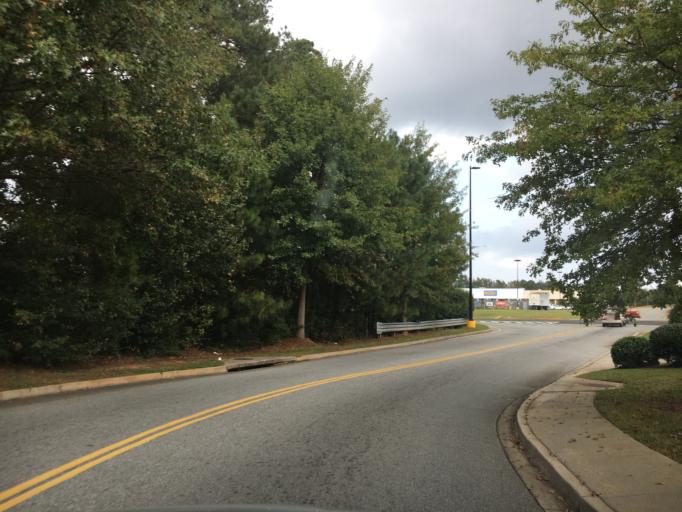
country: US
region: Georgia
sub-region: Hart County
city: Hartwell
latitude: 34.3520
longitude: -82.9054
